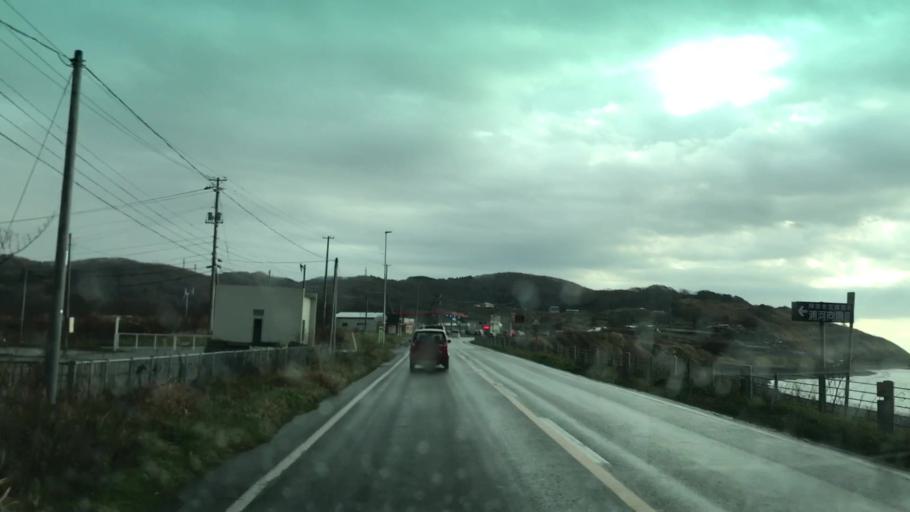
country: JP
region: Hokkaido
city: Shizunai-furukawacho
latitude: 42.1859
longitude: 142.7196
